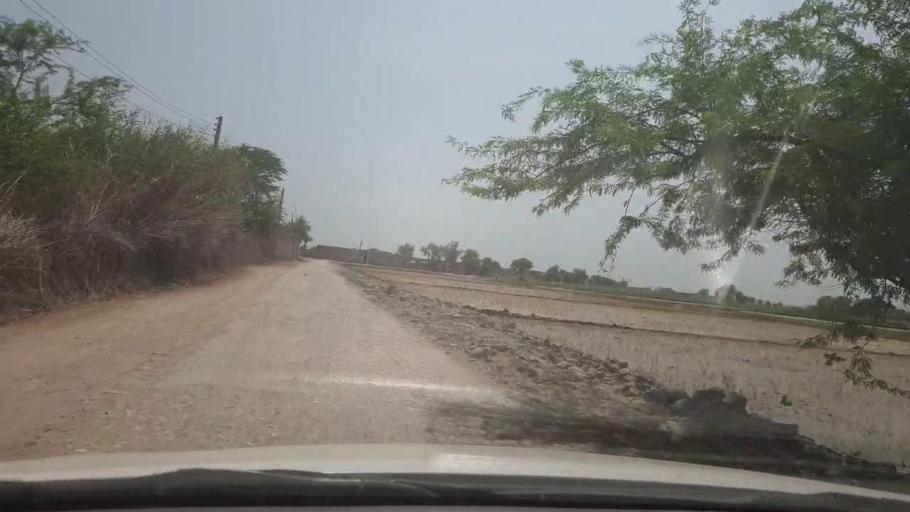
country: PK
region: Sindh
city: Shikarpur
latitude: 27.9981
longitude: 68.5891
